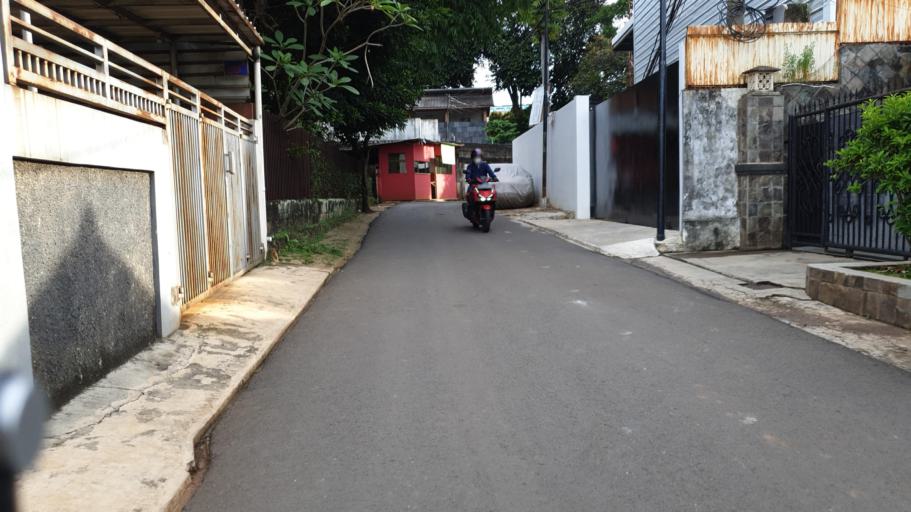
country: ID
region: Banten
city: South Tangerang
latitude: -6.2908
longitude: 106.7882
